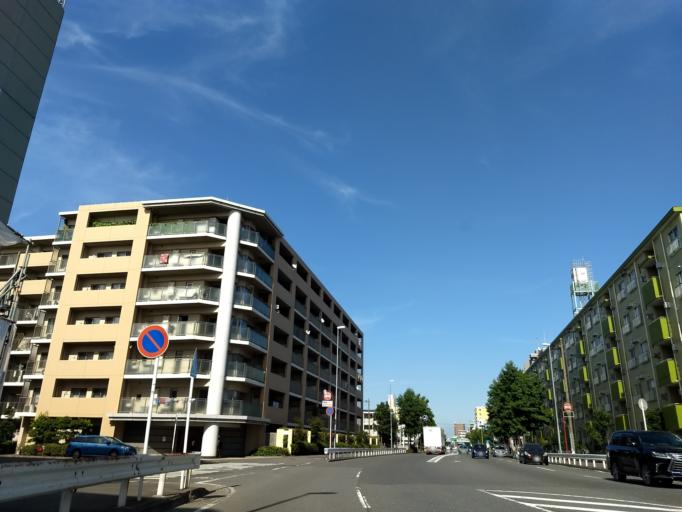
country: JP
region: Kanagawa
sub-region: Kawasaki-shi
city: Kawasaki
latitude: 35.5369
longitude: 139.7281
